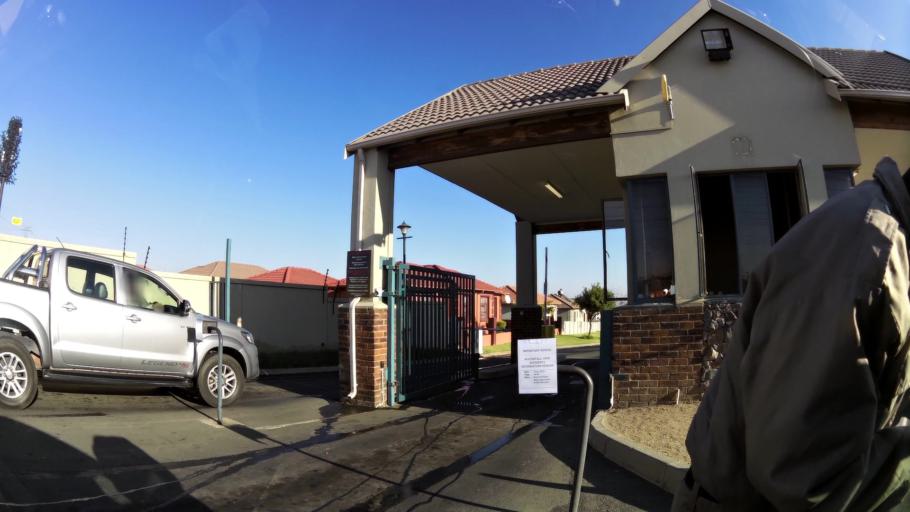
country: ZA
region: Gauteng
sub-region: City of Johannesburg Metropolitan Municipality
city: Modderfontein
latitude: -26.0433
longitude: 28.1462
